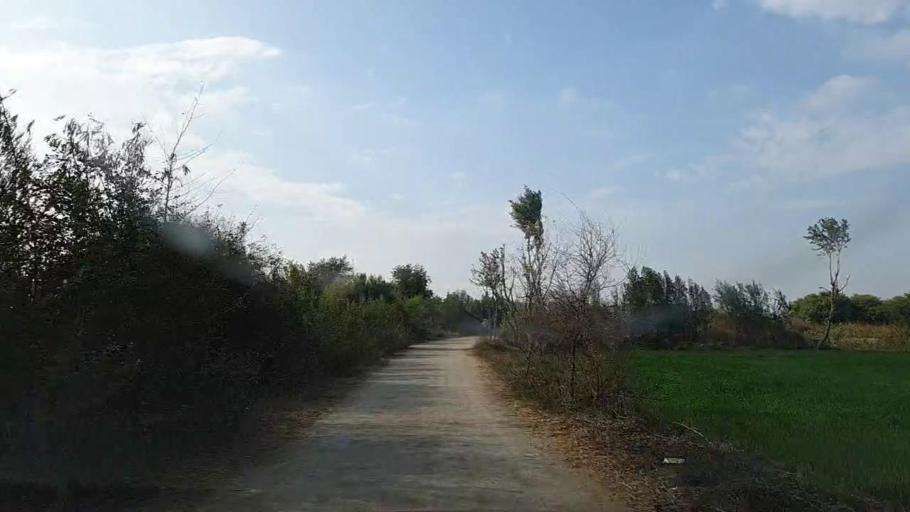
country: PK
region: Sindh
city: Sanghar
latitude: 26.2471
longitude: 69.0151
